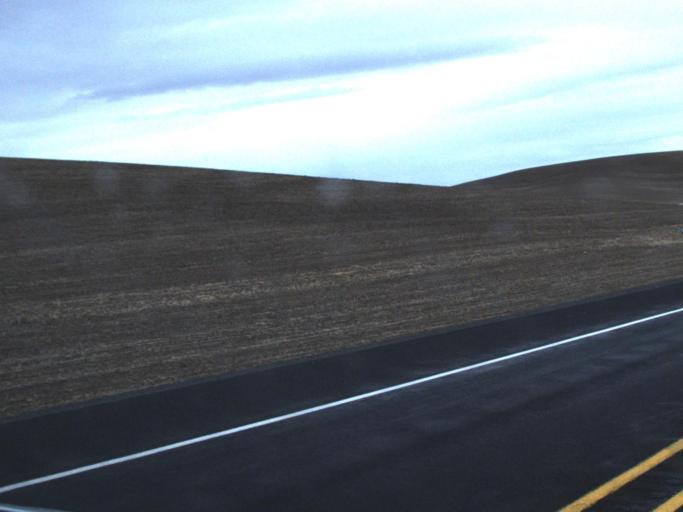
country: US
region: Washington
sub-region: Whitman County
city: Pullman
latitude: 46.6202
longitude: -117.1636
